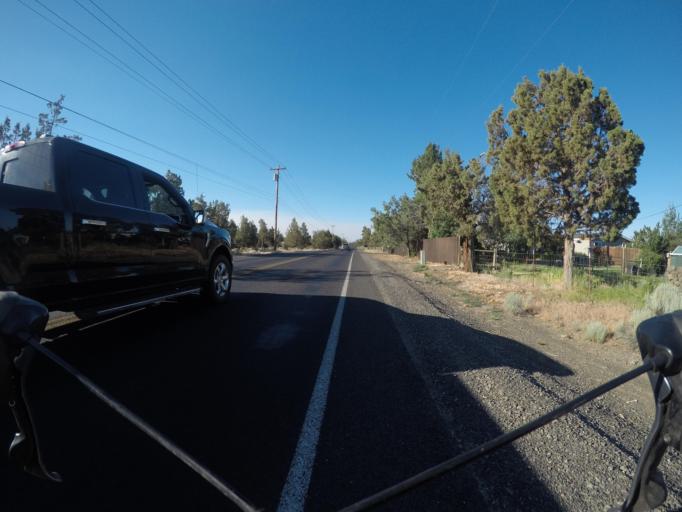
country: US
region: Oregon
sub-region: Deschutes County
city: Redmond
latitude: 44.2290
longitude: -121.2297
